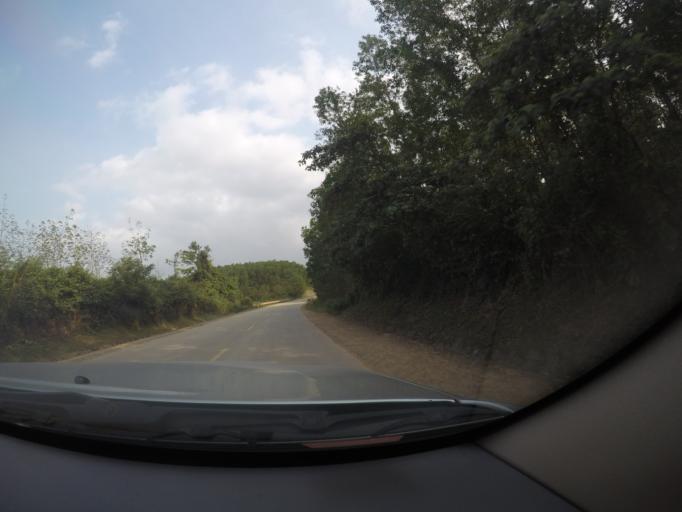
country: VN
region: Quang Binh
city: Kien Giang
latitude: 17.0946
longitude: 106.8533
